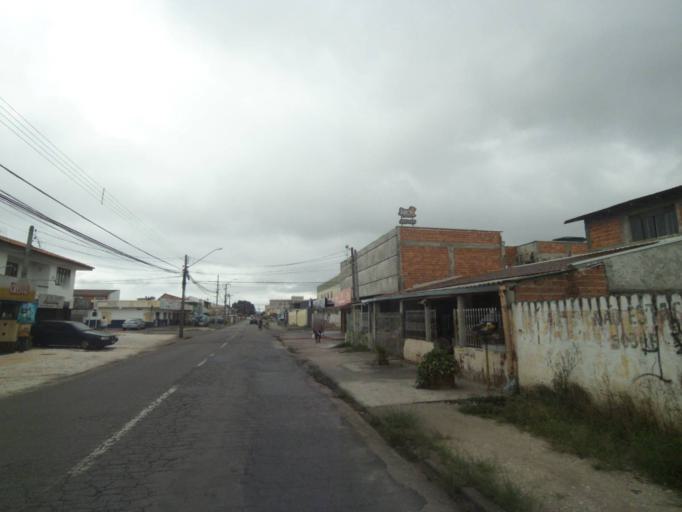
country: BR
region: Parana
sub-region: Pinhais
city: Pinhais
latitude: -25.4452
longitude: -49.1799
